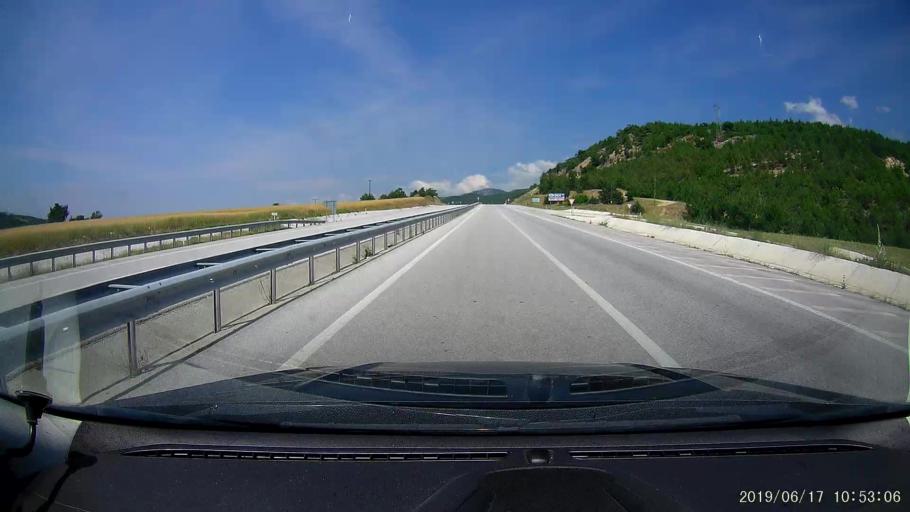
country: TR
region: Corum
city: Hacihamza
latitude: 41.0829
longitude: 34.3295
